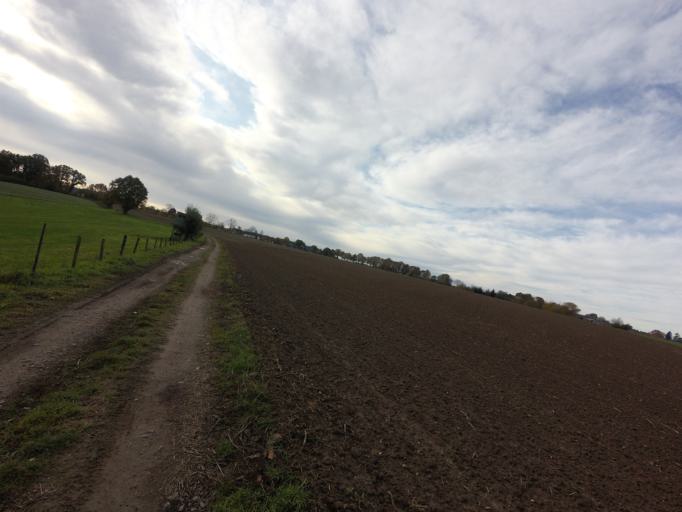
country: BE
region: Flanders
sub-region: Provincie Limburg
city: Sint-Pieters-Voeren
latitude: 50.7765
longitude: 5.8828
